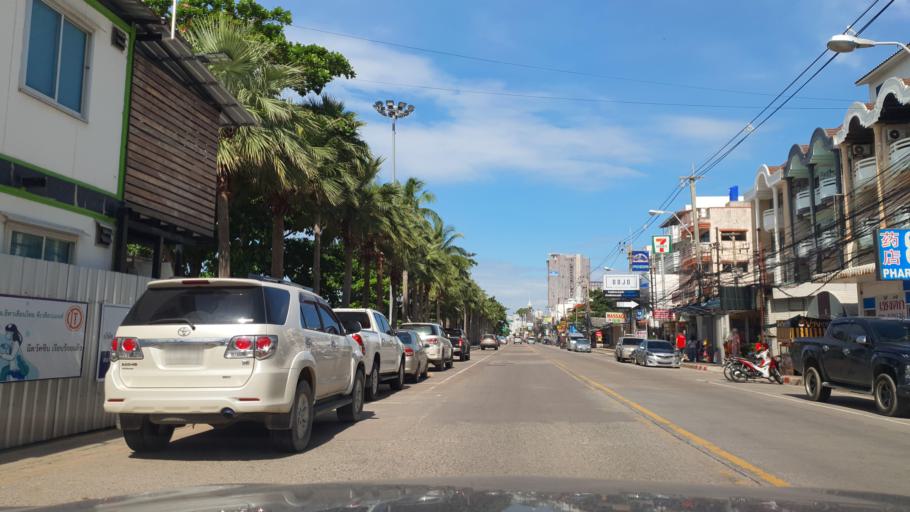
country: TH
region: Chon Buri
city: Phatthaya
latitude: 12.8795
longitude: 100.8834
